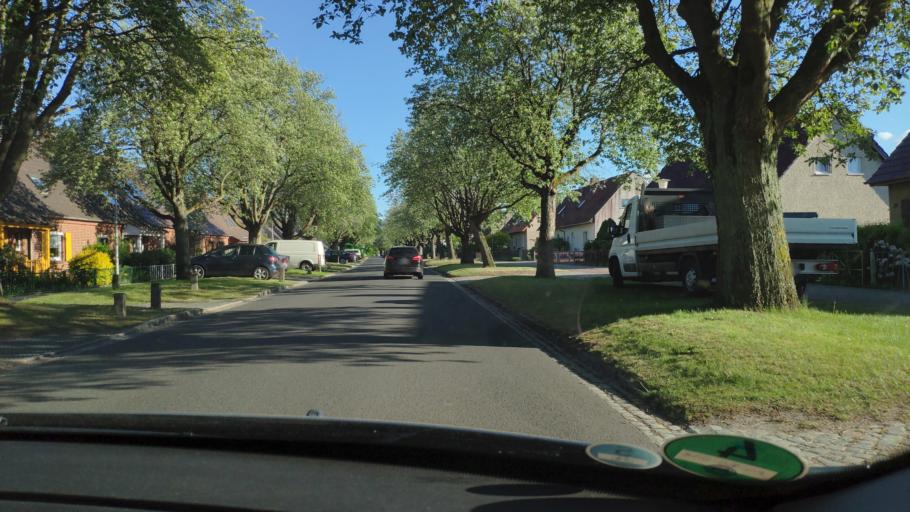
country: DE
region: Mecklenburg-Vorpommern
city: Rechlin
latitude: 53.2825
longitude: 12.8142
